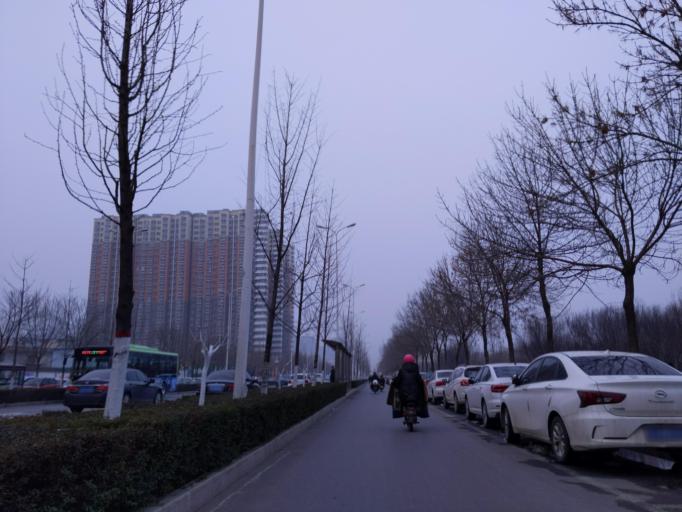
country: CN
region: Henan Sheng
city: Puyang
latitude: 35.7772
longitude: 115.0264
